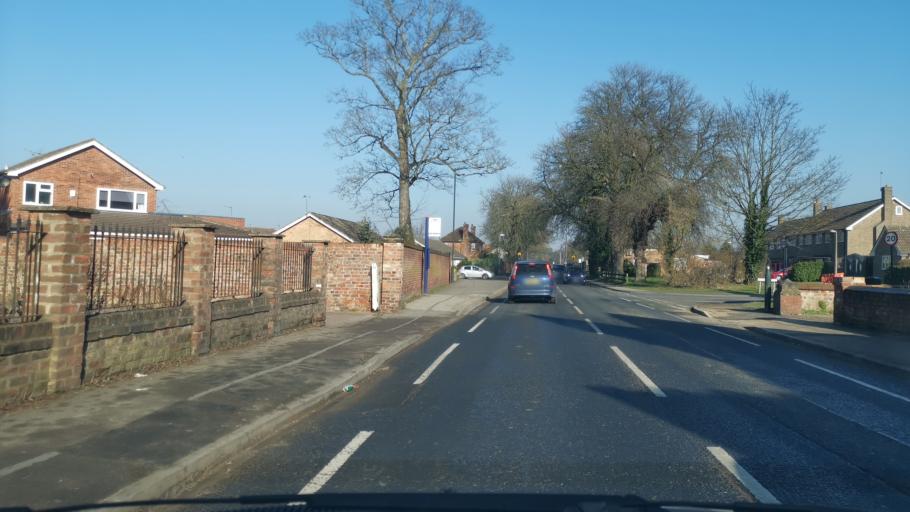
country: GB
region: England
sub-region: City of York
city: Huntington
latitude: 54.0006
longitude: -1.0582
